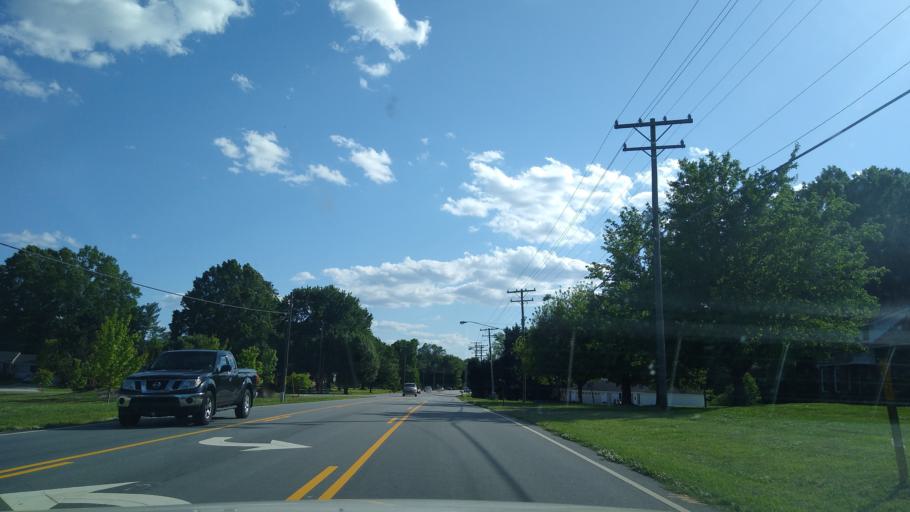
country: US
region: North Carolina
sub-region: Forsyth County
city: Kernersville
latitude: 36.0960
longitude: -80.0872
